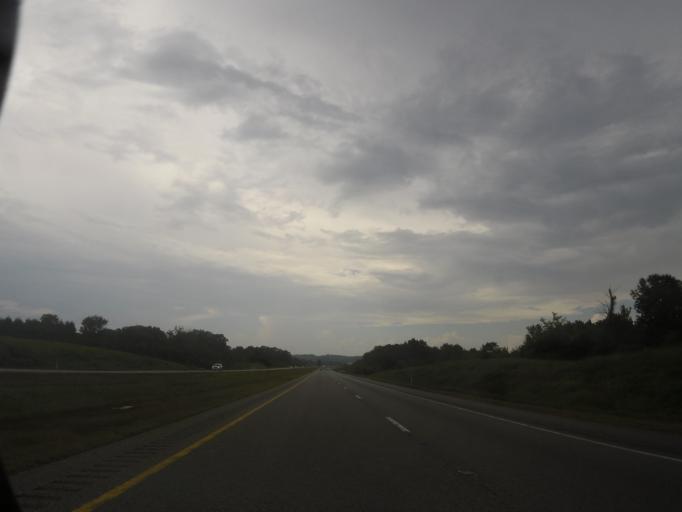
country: US
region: Tennessee
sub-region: Rutherford County
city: Smyrna
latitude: 35.8611
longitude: -86.5645
